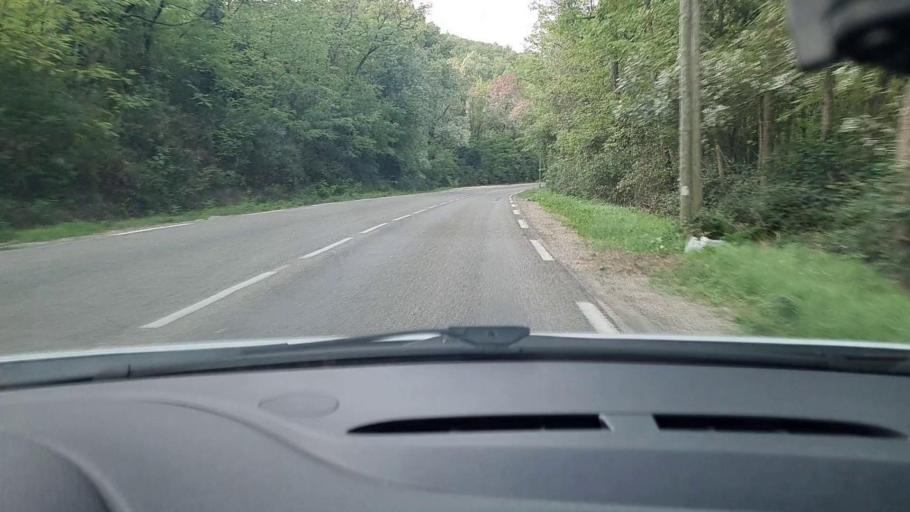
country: FR
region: Languedoc-Roussillon
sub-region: Departement du Gard
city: Saint-Ambroix
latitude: 44.2153
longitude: 4.2633
